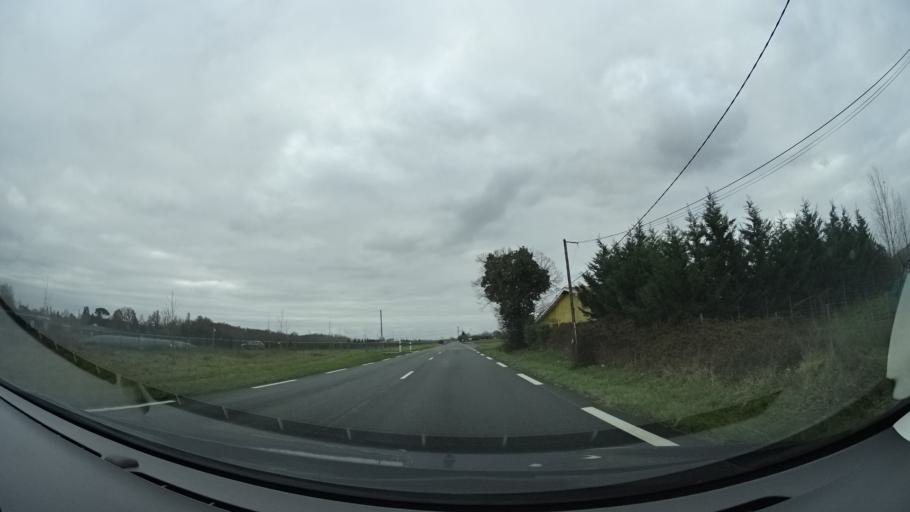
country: FR
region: Aquitaine
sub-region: Departement du Lot-et-Garonne
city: Castelmoron-sur-Lot
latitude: 44.3647
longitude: 0.4568
